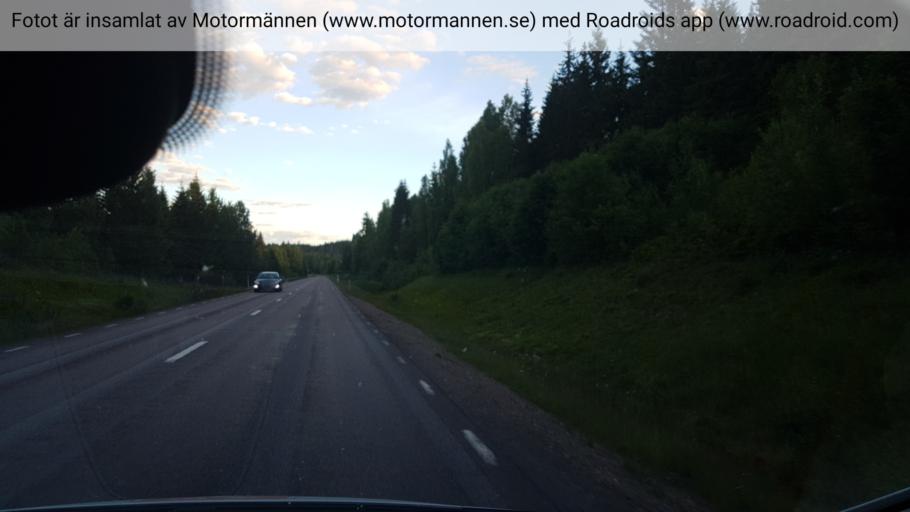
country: SE
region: Vaermland
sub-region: Torsby Kommun
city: Torsby
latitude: 60.0841
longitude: 13.0305
